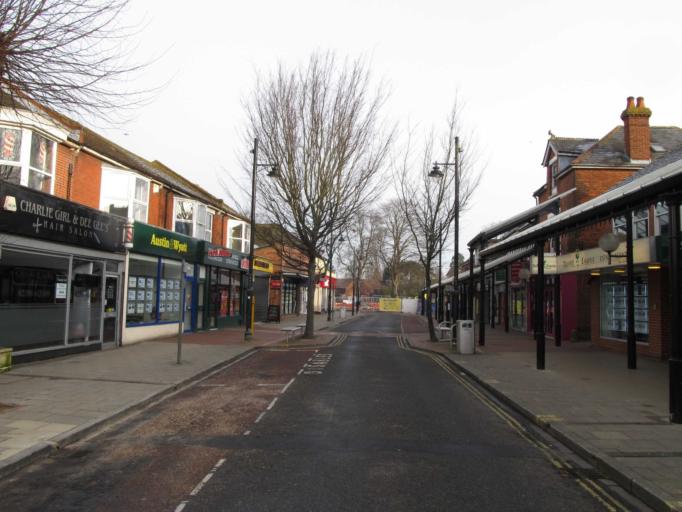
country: GB
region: England
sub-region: Hampshire
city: Eastleigh
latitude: 50.9687
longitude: -1.3535
